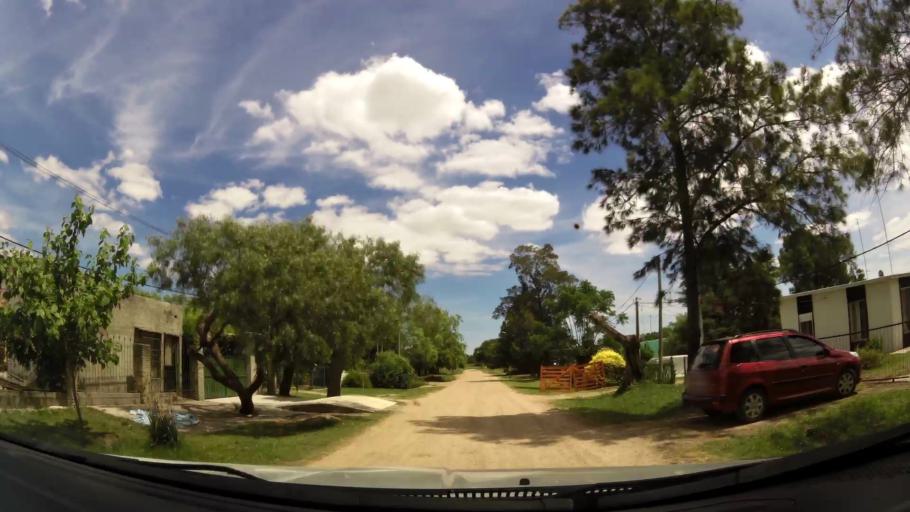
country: UY
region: San Jose
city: Delta del Tigre
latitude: -34.7410
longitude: -56.4370
